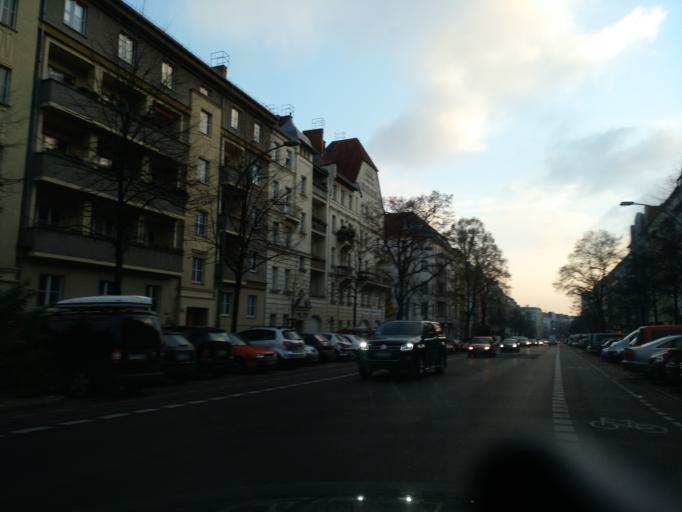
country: DE
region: Berlin
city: Friedrichshain Bezirk
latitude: 52.5187
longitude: 13.4619
